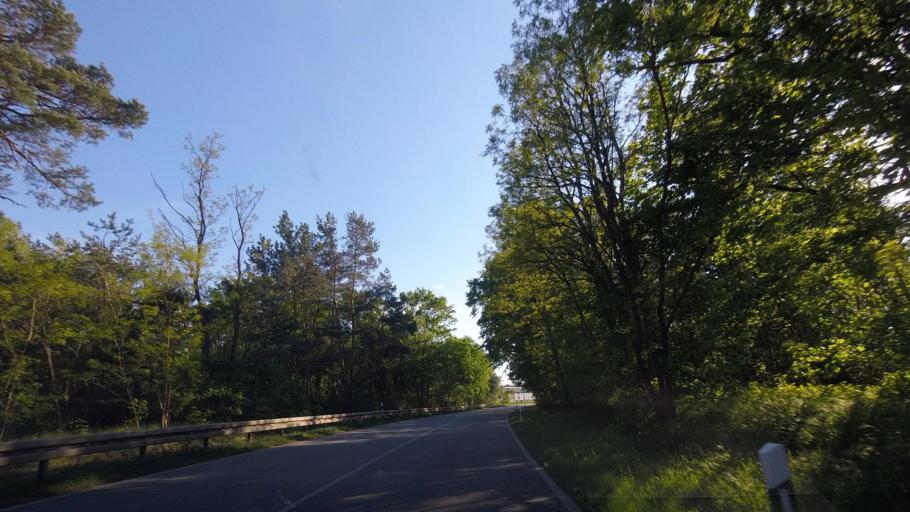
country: DE
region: Brandenburg
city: Luebben
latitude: 51.9086
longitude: 13.8620
